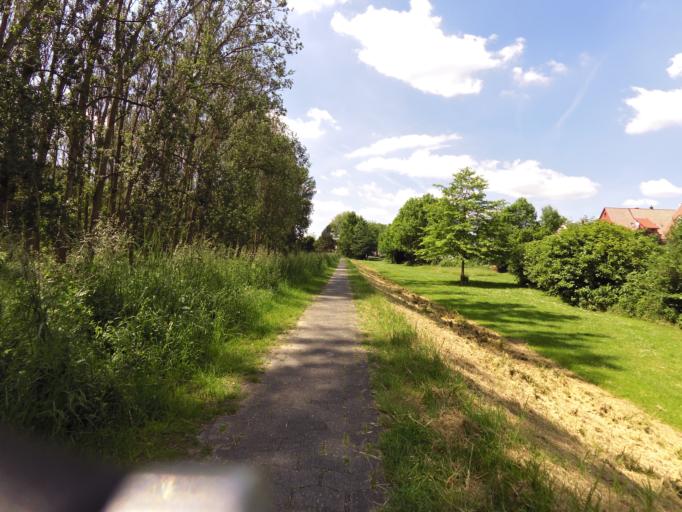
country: DE
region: Hesse
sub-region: Regierungsbezirk Darmstadt
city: Trebur
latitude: 49.9226
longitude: 8.4109
